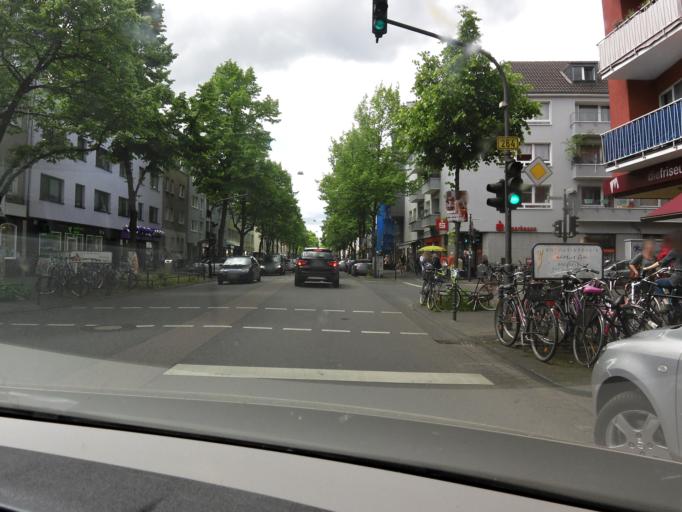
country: DE
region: North Rhine-Westphalia
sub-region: Regierungsbezirk Koln
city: Neustadt/Sued
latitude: 50.9303
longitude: 6.9153
